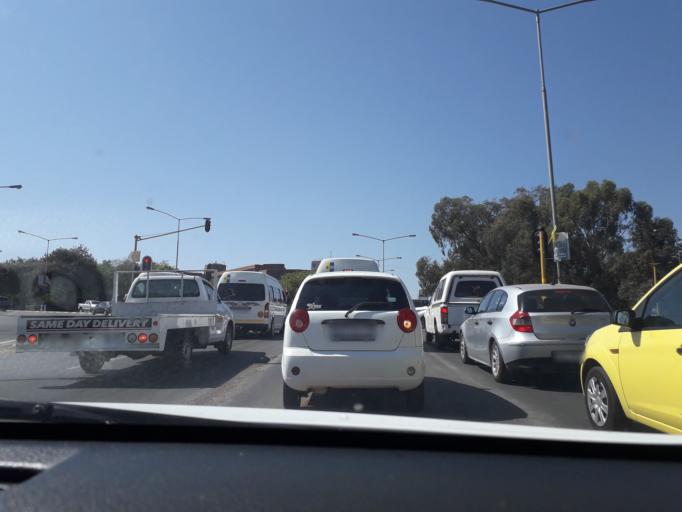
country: ZA
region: Gauteng
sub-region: City of Johannesburg Metropolitan Municipality
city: Modderfontein
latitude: -26.1006
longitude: 28.2248
